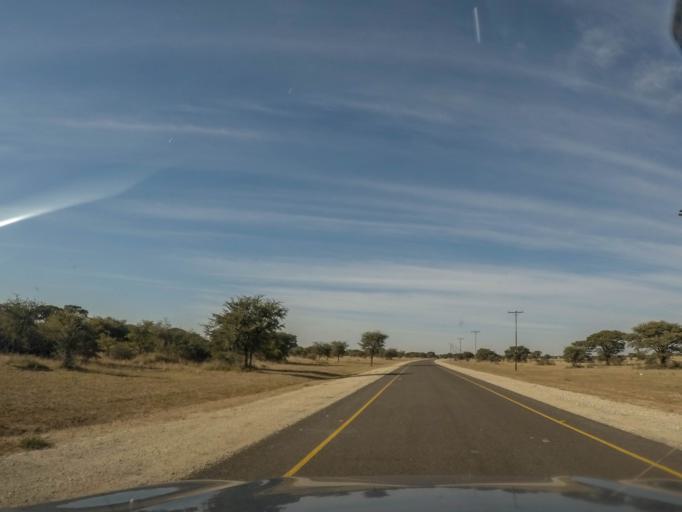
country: BW
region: South East
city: Janeng
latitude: -25.5646
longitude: 25.3081
